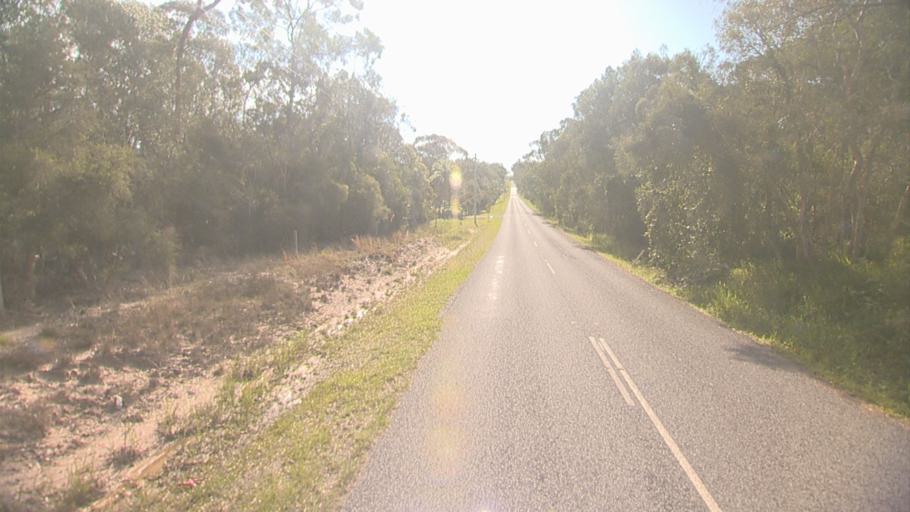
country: AU
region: Queensland
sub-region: Logan
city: Logan Reserve
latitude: -27.7339
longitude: 153.0869
